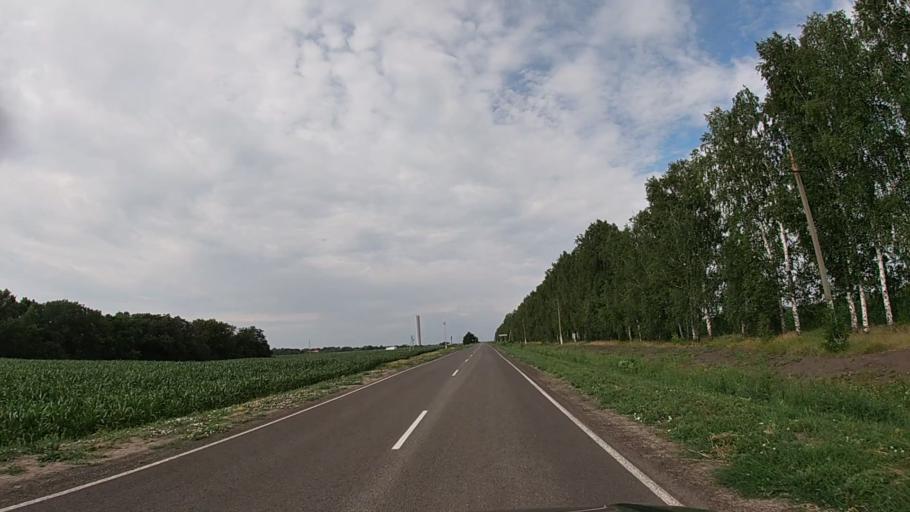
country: UA
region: Sumy
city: Krasnopillya
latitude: 50.8199
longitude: 35.4561
